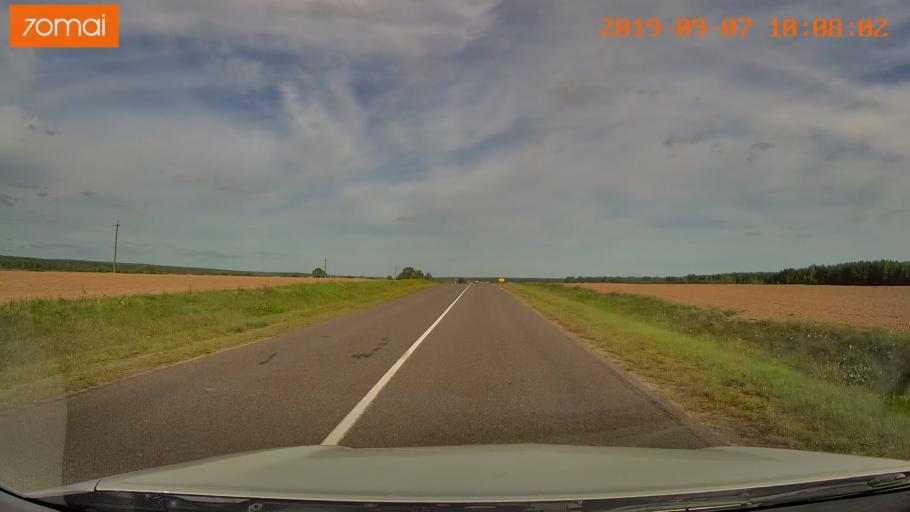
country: BY
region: Grodnenskaya
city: Voranava
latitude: 54.0830
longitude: 25.3927
